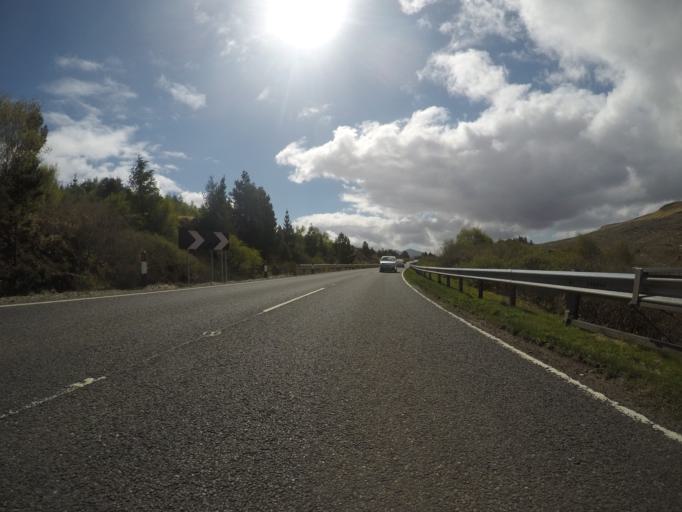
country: GB
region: Scotland
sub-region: Highland
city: Isle of Skye
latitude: 57.3435
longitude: -6.1974
